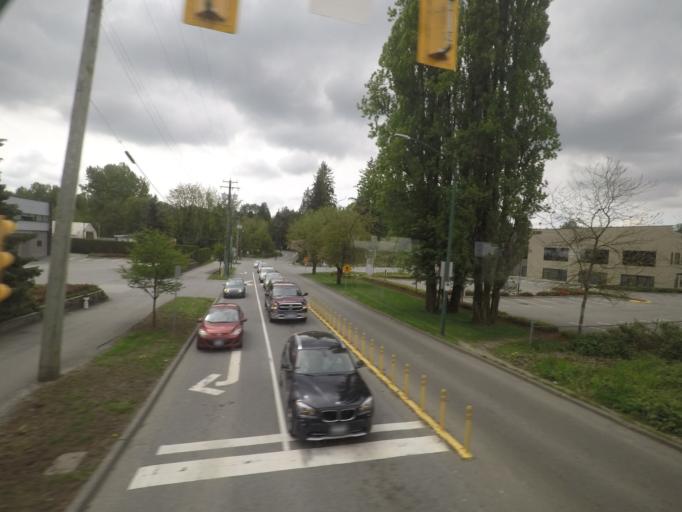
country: CA
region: British Columbia
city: Burnaby
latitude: 49.2505
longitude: -122.9141
